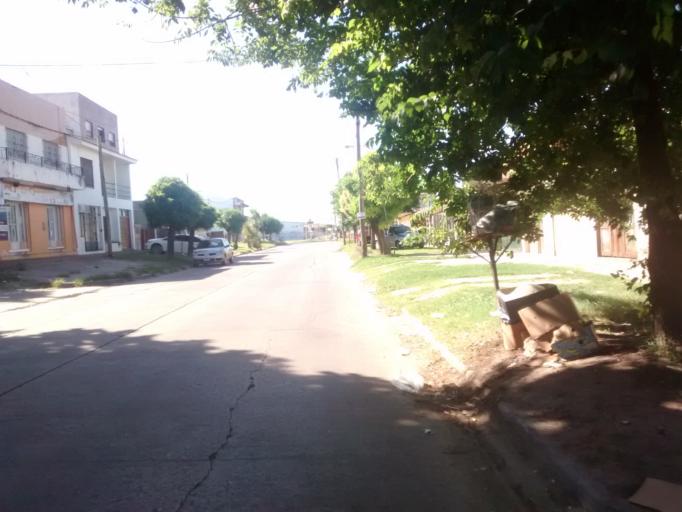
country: AR
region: Buenos Aires
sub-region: Partido de La Plata
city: La Plata
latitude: -34.9279
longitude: -57.9071
